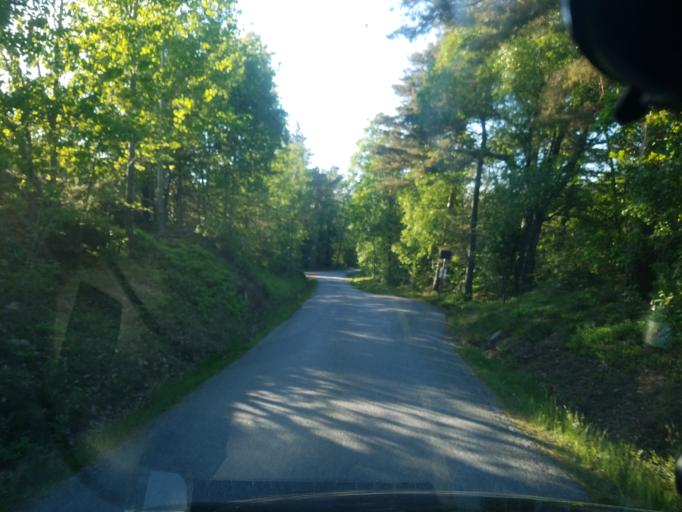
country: SE
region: Vaestra Goetaland
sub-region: Lysekils Kommun
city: Lysekil
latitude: 58.3029
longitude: 11.4637
